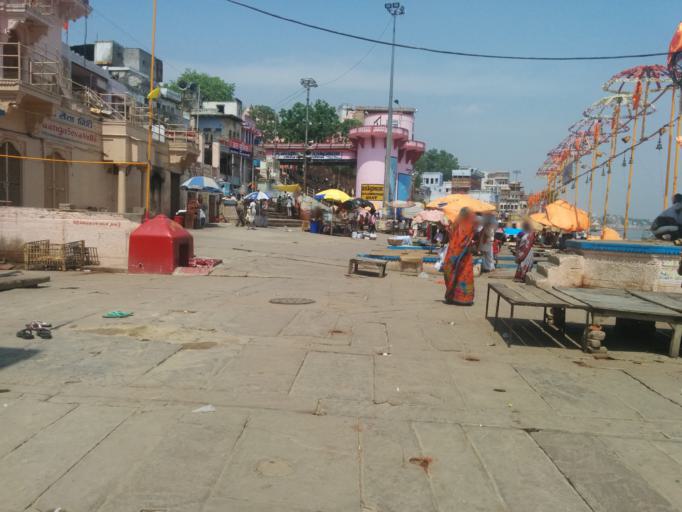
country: IN
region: Uttar Pradesh
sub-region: Varanasi
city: Varanasi
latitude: 25.3066
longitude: 83.0104
